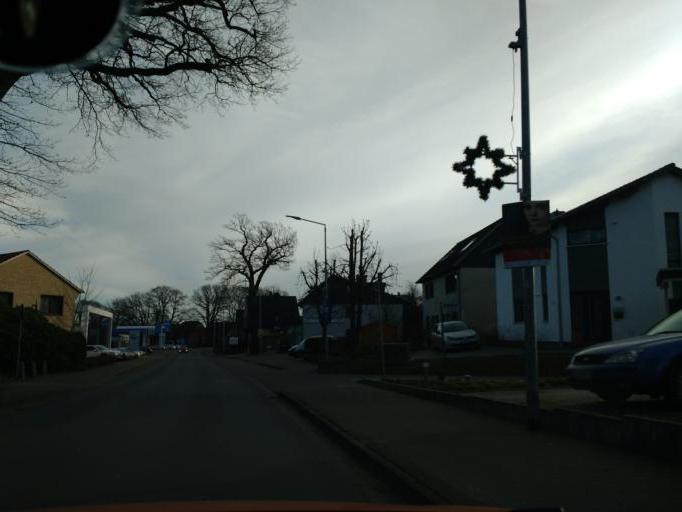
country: DE
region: Lower Saxony
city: Hude
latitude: 53.1100
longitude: 8.4630
